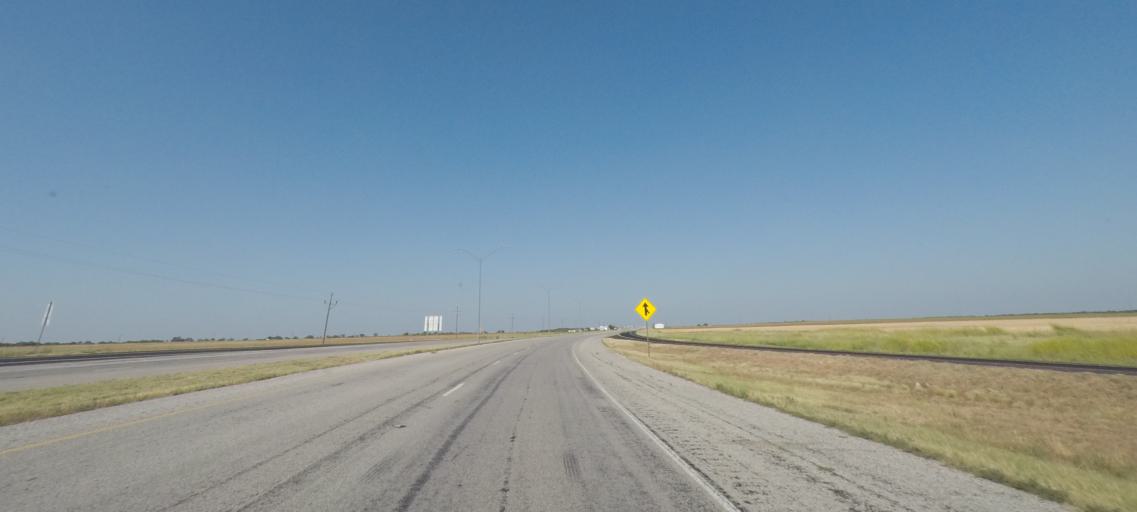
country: US
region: Texas
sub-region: Baylor County
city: Seymour
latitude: 33.6186
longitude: -99.2402
